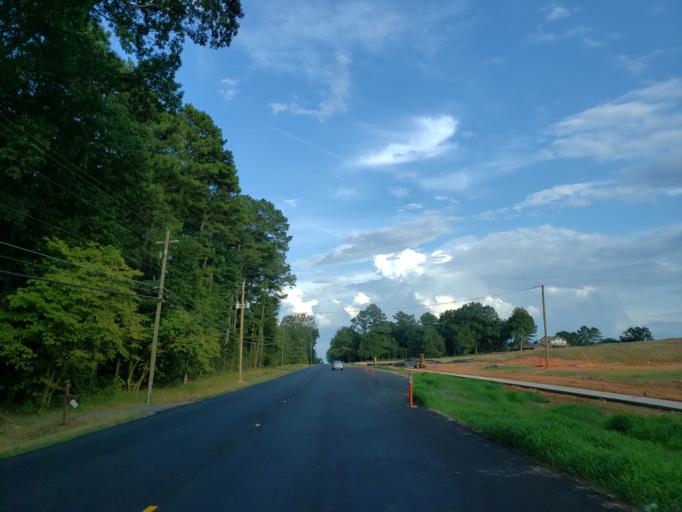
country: US
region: Georgia
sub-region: Bartow County
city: Cartersville
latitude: 34.2382
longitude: -84.8750
